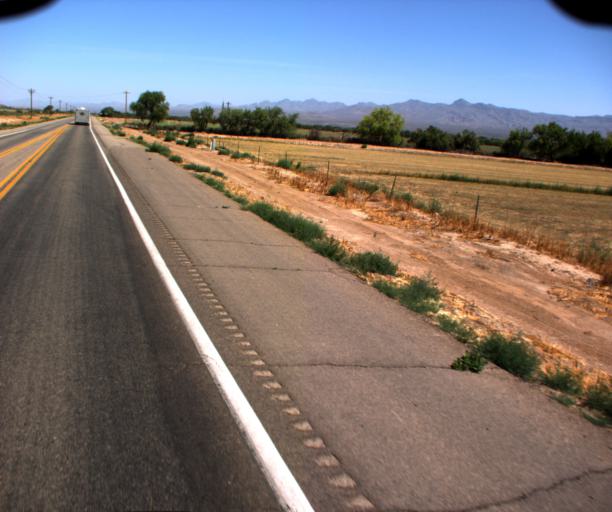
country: US
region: Arizona
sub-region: Graham County
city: Pima
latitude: 32.9632
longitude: -109.9209
